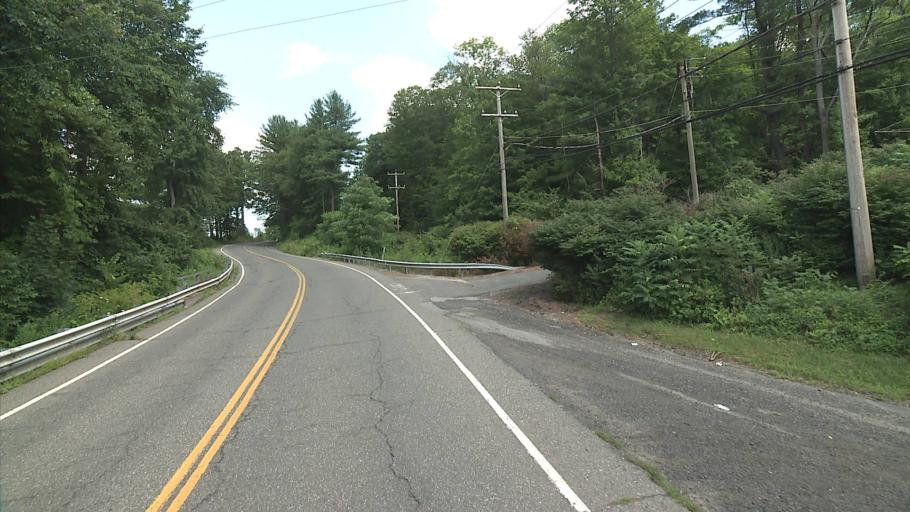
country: US
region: Connecticut
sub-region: Litchfield County
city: Winsted
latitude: 41.9474
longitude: -73.0467
